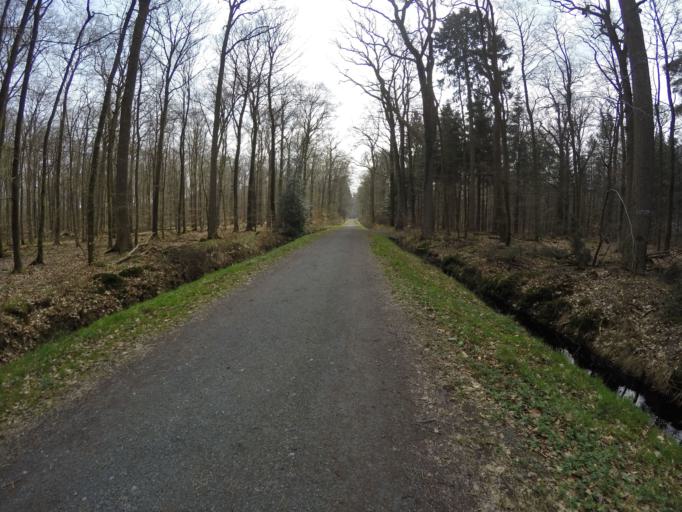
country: DE
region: Schleswig-Holstein
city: Ellerhoop
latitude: 53.7171
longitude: 9.7980
